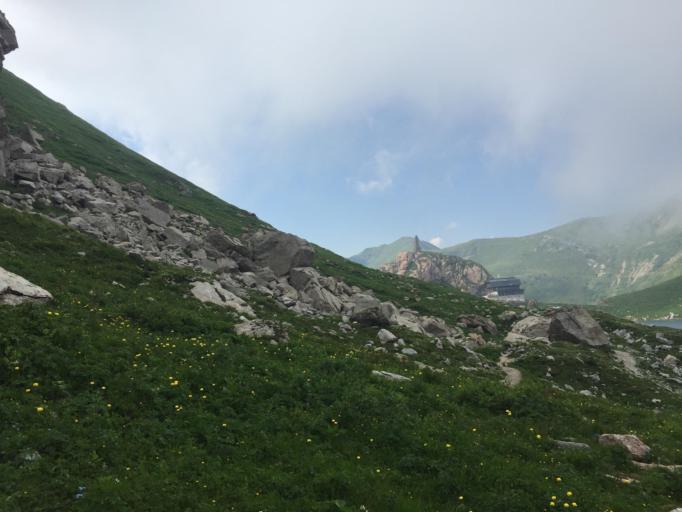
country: IT
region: Friuli Venezia Giulia
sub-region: Provincia di Udine
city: Rigolato
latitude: 46.6093
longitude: 12.8679
